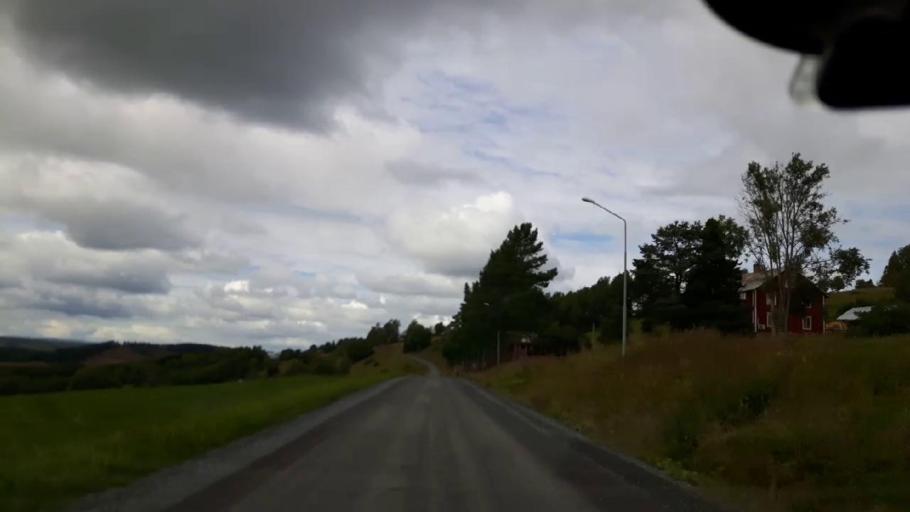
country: SE
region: Jaemtland
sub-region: Krokoms Kommun
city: Valla
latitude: 63.4984
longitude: 13.9716
